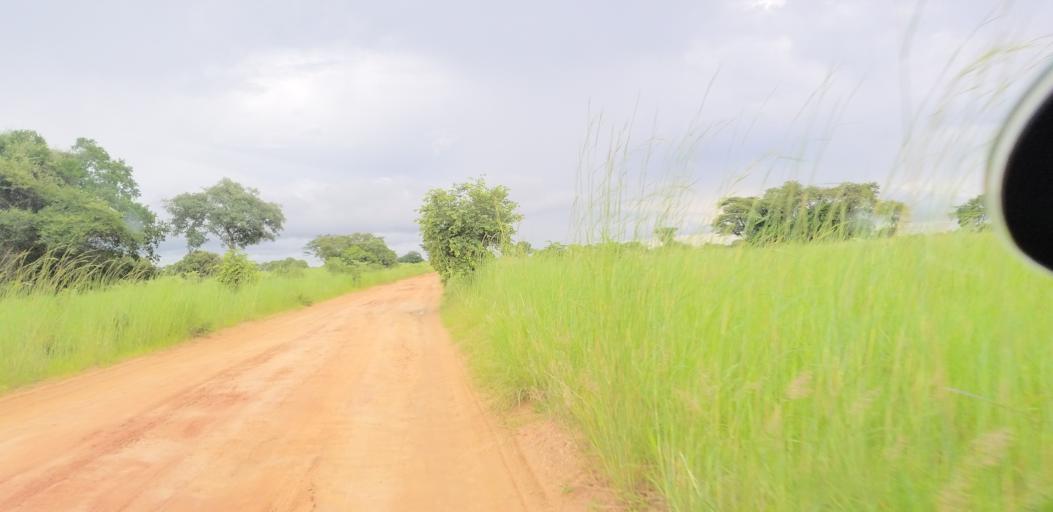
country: ZM
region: Lusaka
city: Chongwe
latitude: -15.1670
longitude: 28.4701
